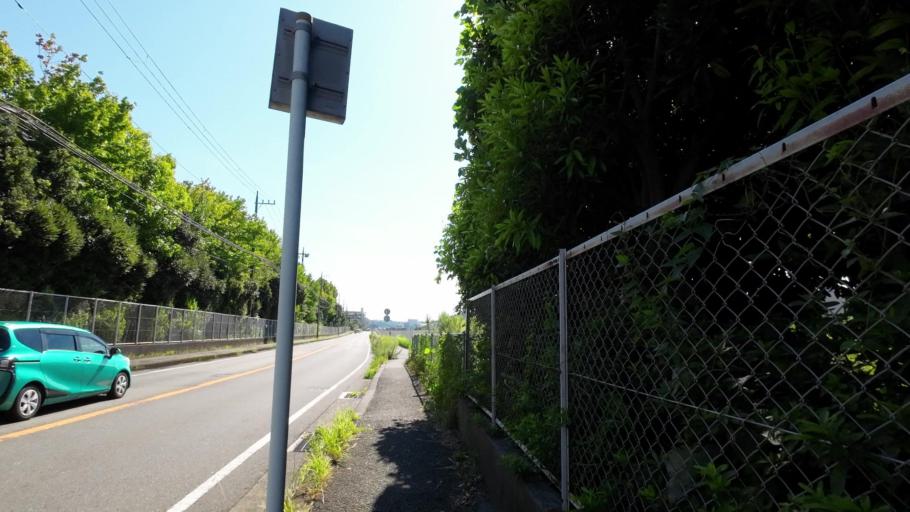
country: JP
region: Kanagawa
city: Fujisawa
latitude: 35.3460
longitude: 139.5144
